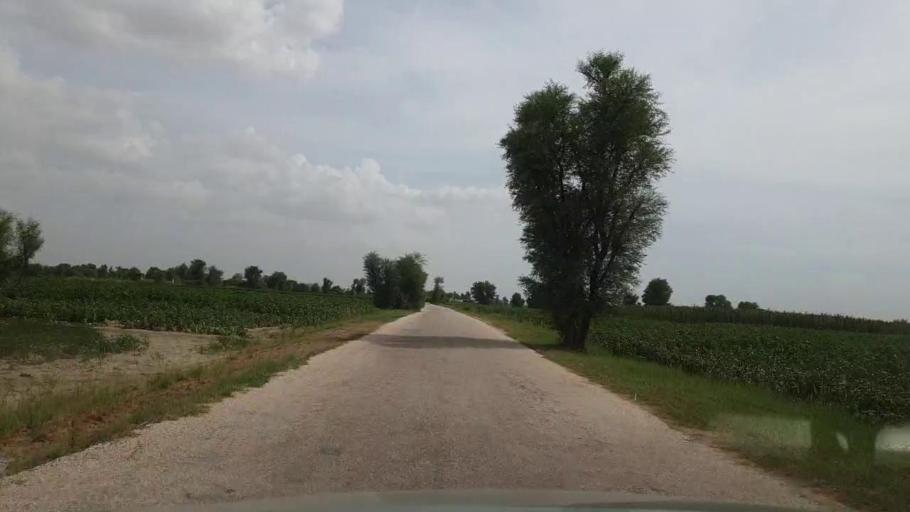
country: PK
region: Sindh
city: Kot Diji
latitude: 27.1415
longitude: 69.0281
